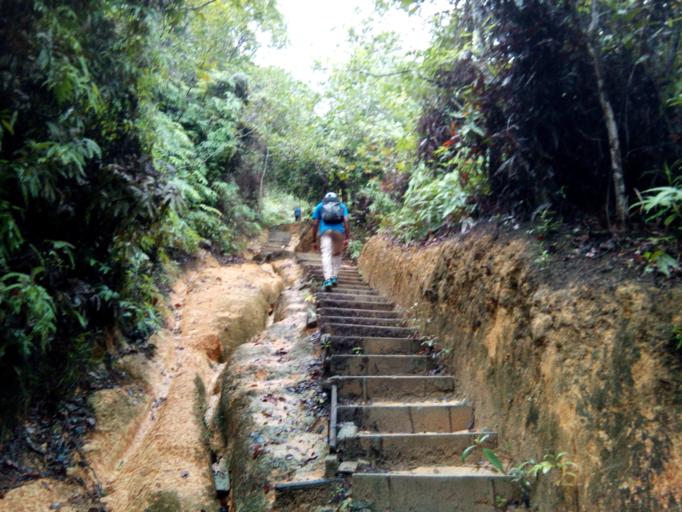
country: MY
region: Penang
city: Tanjung Tokong
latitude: 5.4312
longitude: 100.2909
